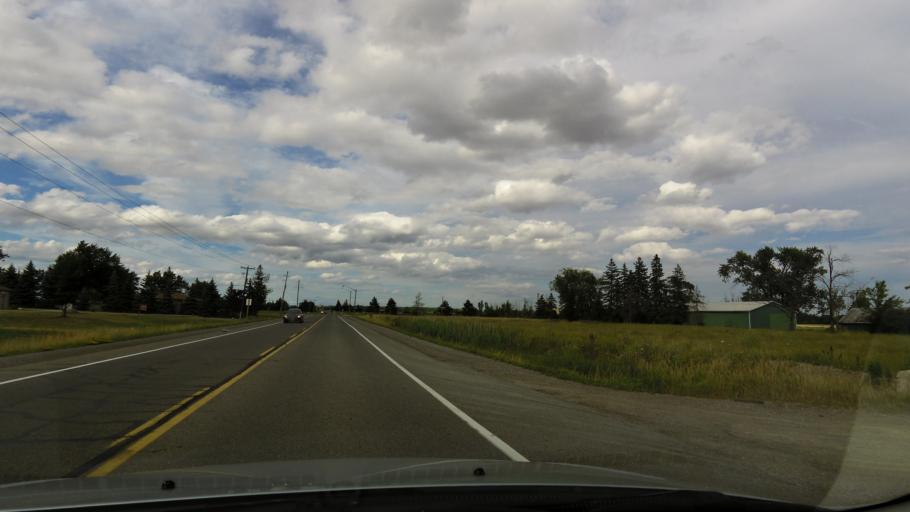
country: CA
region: Ontario
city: Brampton
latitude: 43.6835
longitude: -79.8785
